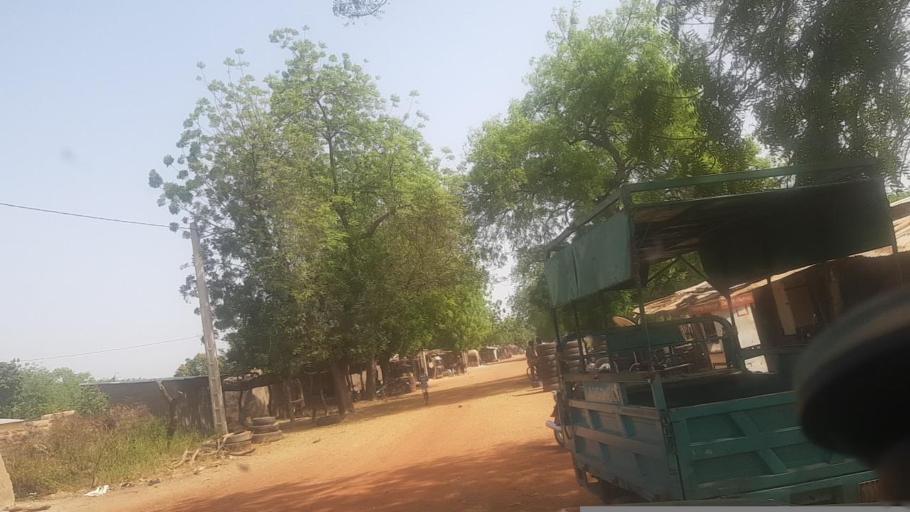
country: ML
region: Segou
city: Bla
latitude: 12.9116
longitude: -6.2417
